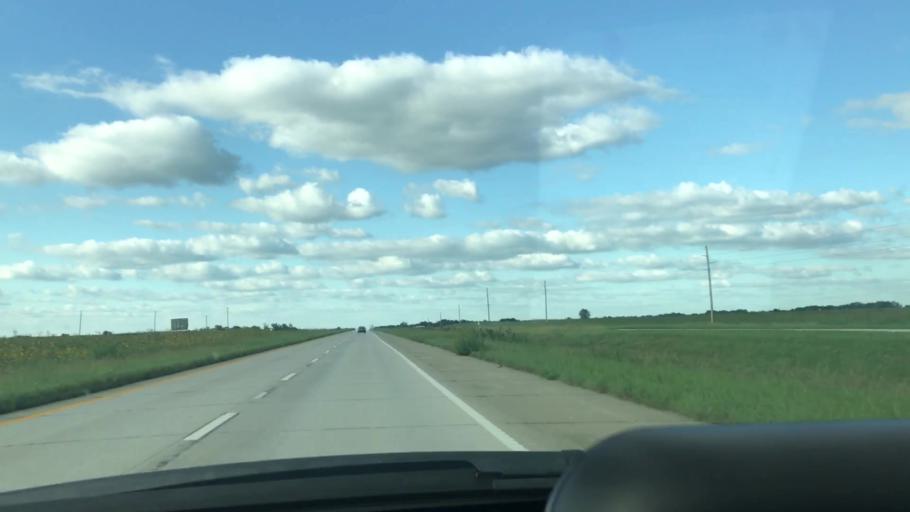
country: US
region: Missouri
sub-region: Benton County
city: Cole Camp
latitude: 38.5127
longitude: -93.2726
